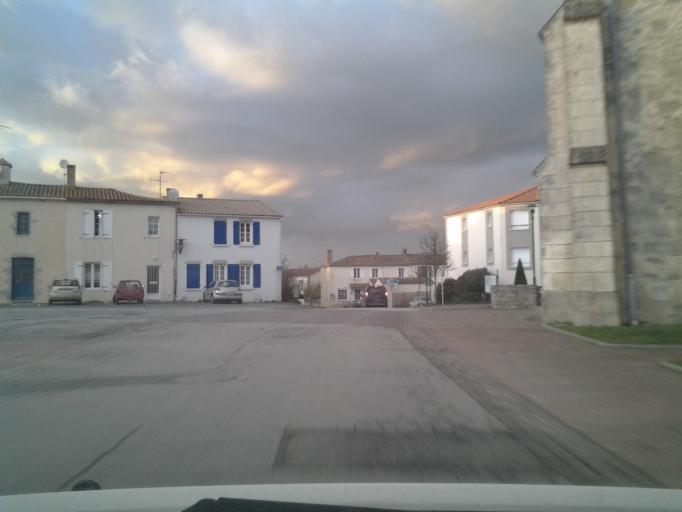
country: FR
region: Pays de la Loire
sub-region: Departement de la Vendee
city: Les Clouzeaux
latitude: 46.6291
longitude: -1.5084
